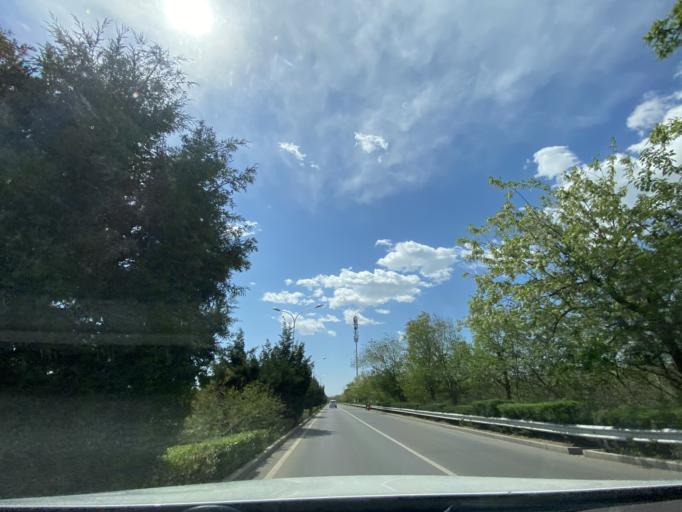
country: CN
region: Beijing
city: Sijiqing
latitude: 39.9519
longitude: 116.2415
